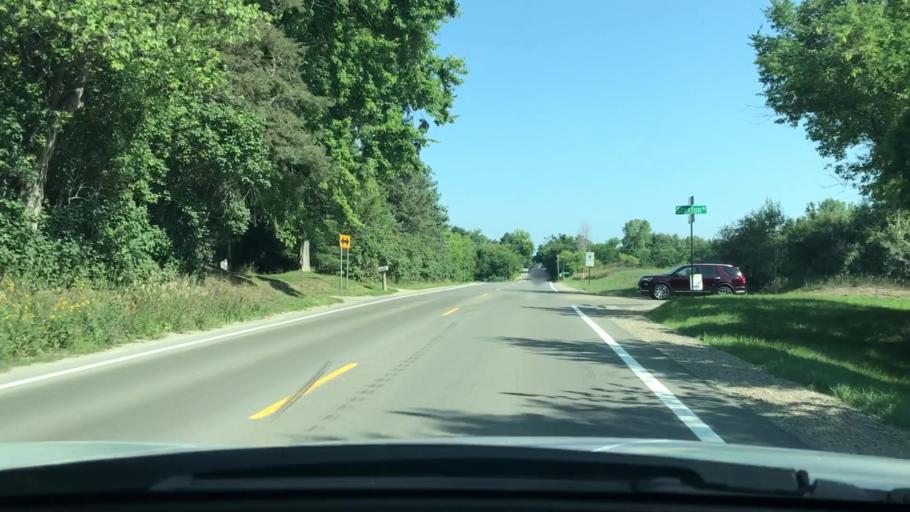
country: US
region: Michigan
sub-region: Oakland County
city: Oxford
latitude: 42.7948
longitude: -83.3330
